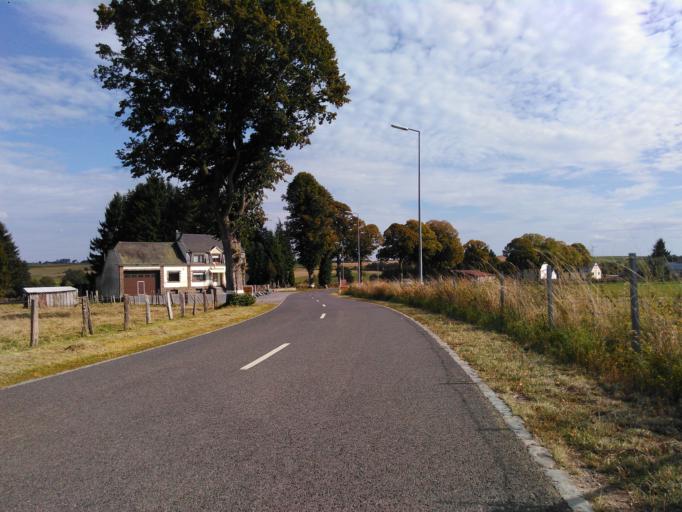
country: LU
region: Diekirch
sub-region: Canton de Clervaux
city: Troisvierges
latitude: 50.1490
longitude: 5.9798
